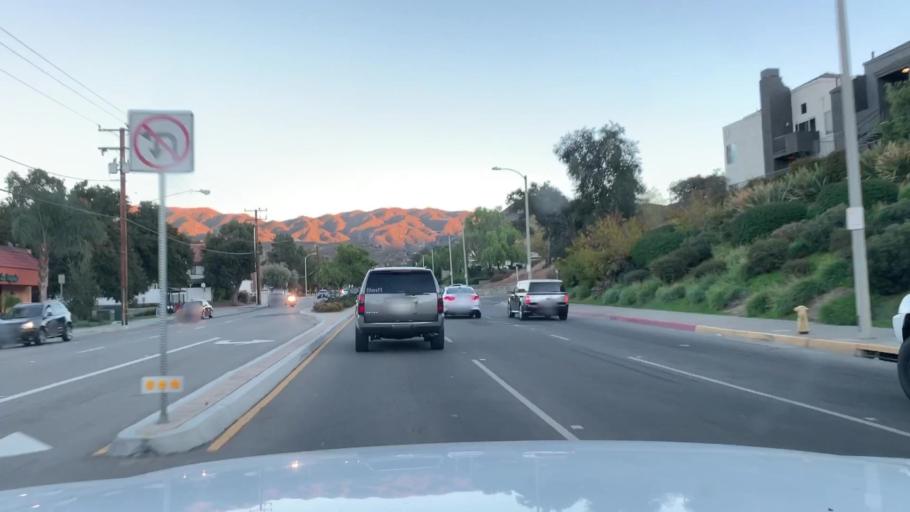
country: US
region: California
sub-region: Los Angeles County
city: Santa Clarita
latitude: 34.3698
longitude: -118.5132
